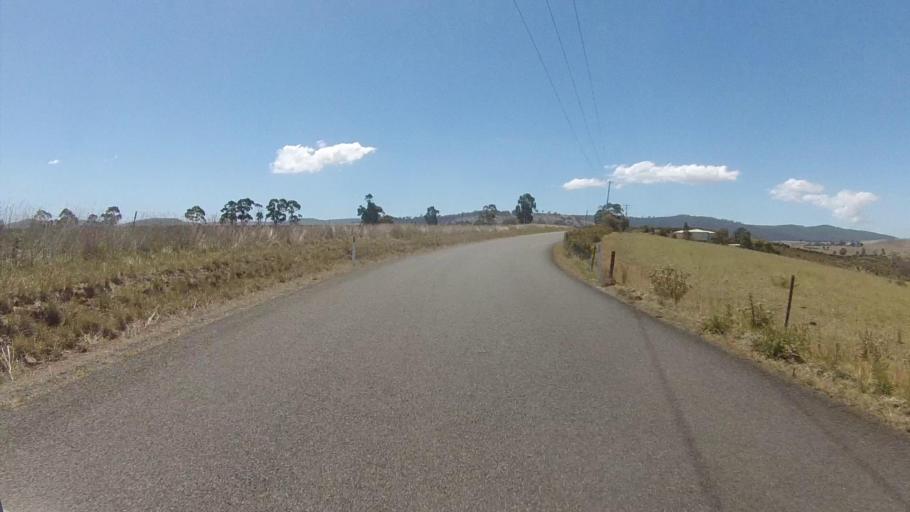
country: AU
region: Tasmania
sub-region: Sorell
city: Sorell
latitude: -42.7754
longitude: 147.5808
